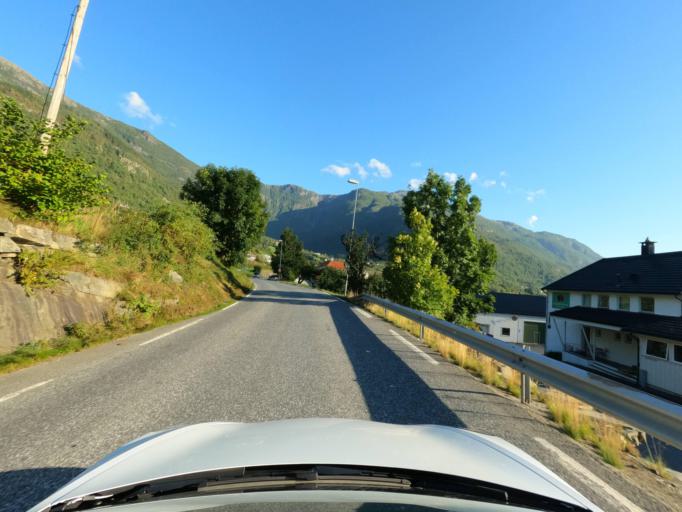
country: NO
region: Hordaland
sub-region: Ullensvang
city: Kinsarvik
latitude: 60.3306
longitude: 6.6545
